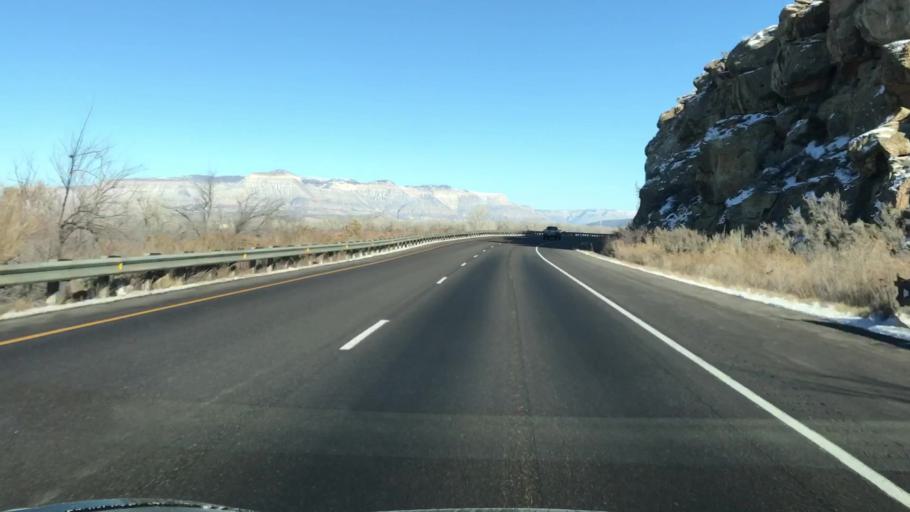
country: US
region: Colorado
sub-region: Mesa County
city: Palisade
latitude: 39.2717
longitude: -108.2481
